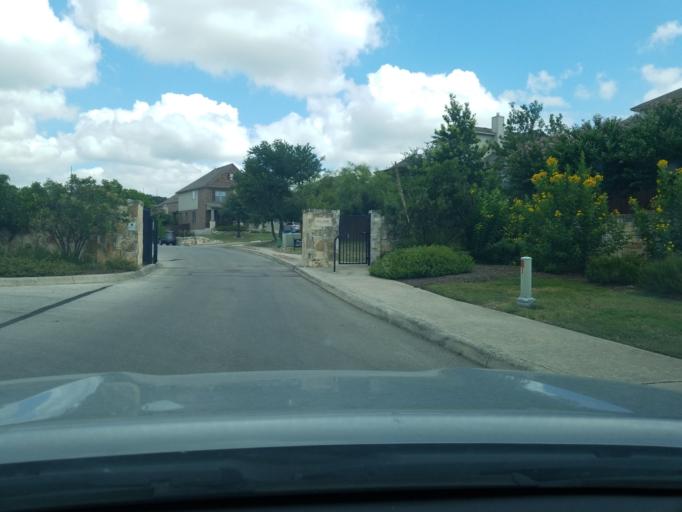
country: US
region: Texas
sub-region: Bexar County
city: Timberwood Park
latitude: 29.6623
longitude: -98.5105
